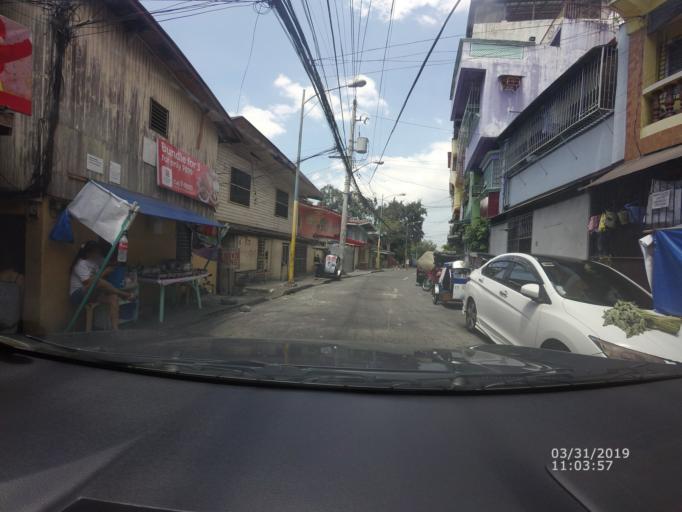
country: PH
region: Metro Manila
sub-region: Mandaluyong
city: Mandaluyong City
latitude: 14.5778
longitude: 121.0416
